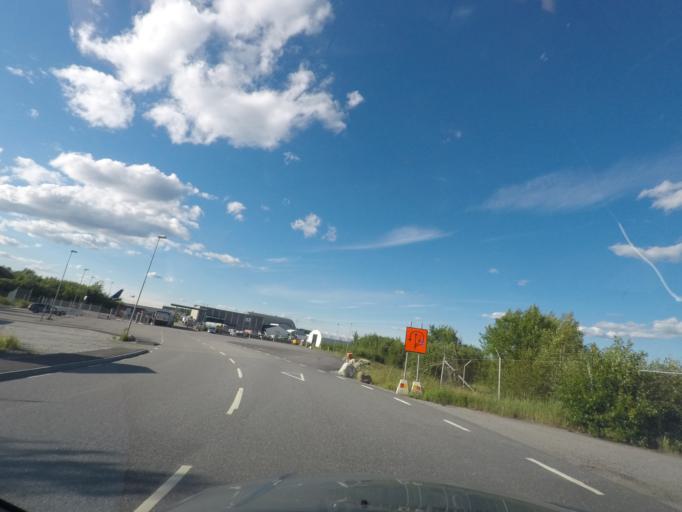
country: SE
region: Stockholm
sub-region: Sigtuna Kommun
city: Rosersberg
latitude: 59.6552
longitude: 17.9578
